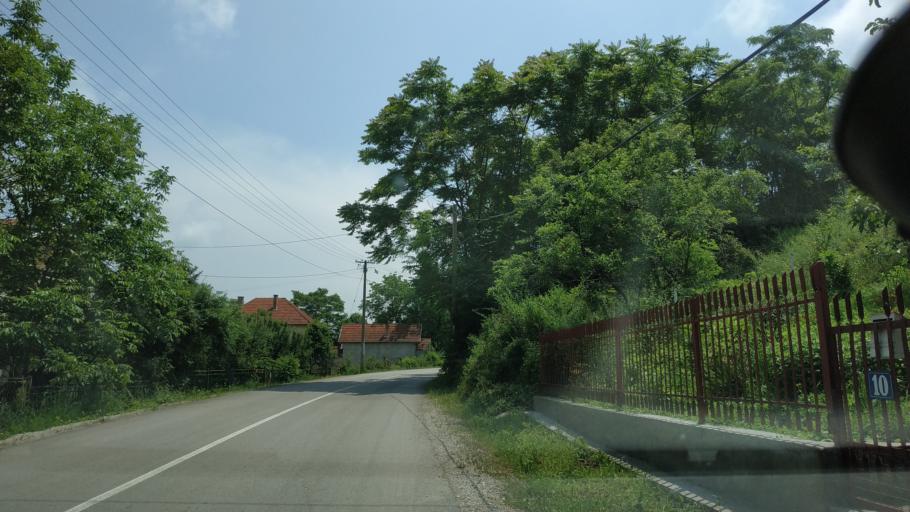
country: RS
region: Central Serbia
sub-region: Nisavski Okrug
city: Aleksinac
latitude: 43.4294
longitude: 21.7436
